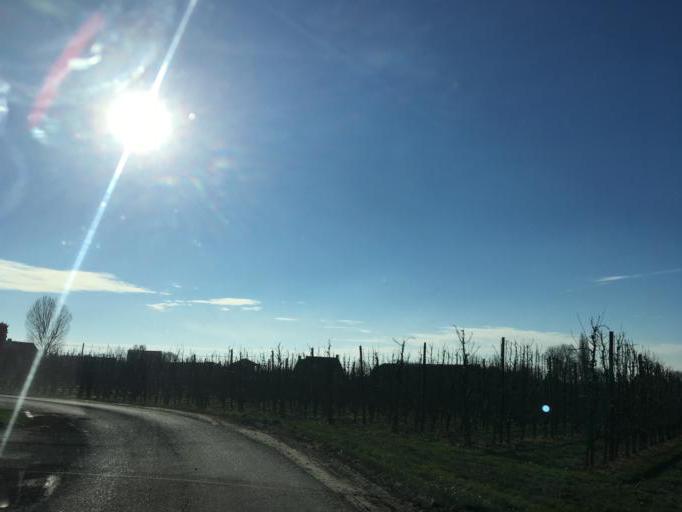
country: BE
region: Flanders
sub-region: Provincie West-Vlaanderen
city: Tielt
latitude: 50.9992
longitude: 3.3041
